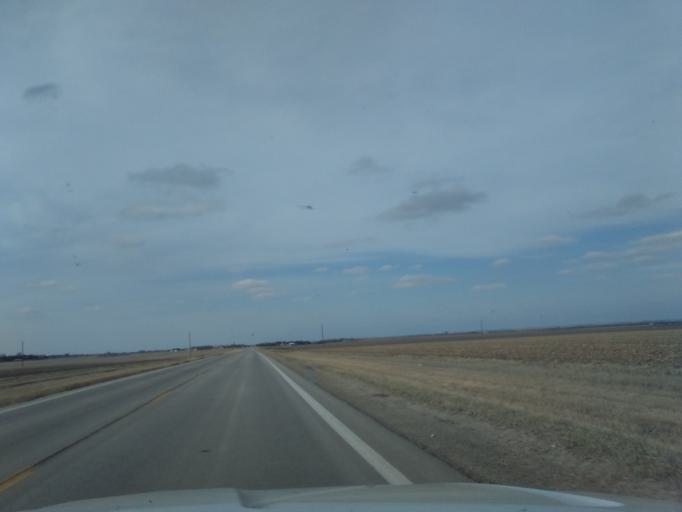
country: US
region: Nebraska
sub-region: Saline County
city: Wilber
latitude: 40.3187
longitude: -96.9162
